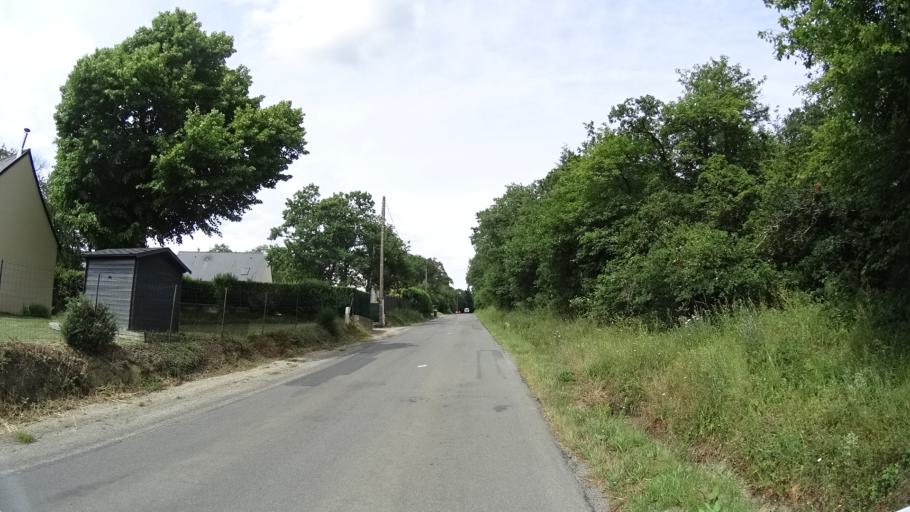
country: FR
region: Brittany
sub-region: Departement d'Ille-et-Vilaine
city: Laille
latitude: 47.9709
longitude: -1.7235
